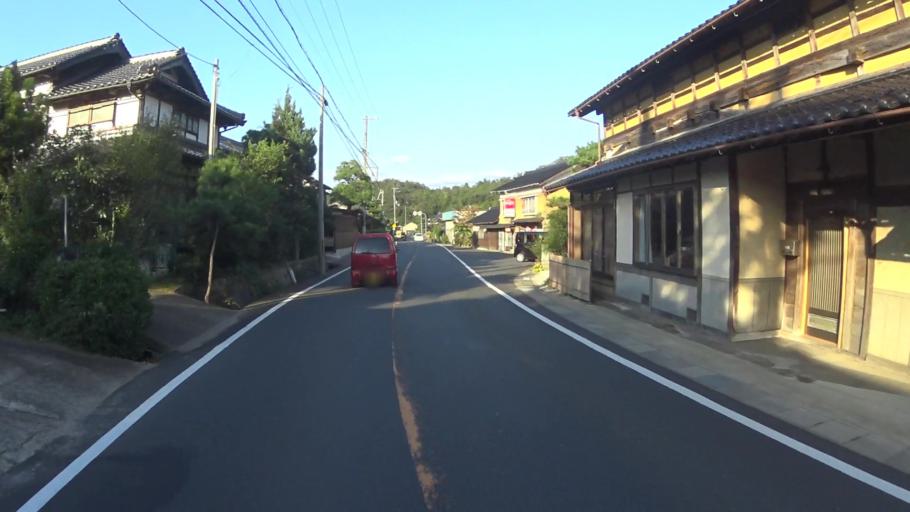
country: JP
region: Kyoto
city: Miyazu
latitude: 35.5923
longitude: 135.0407
